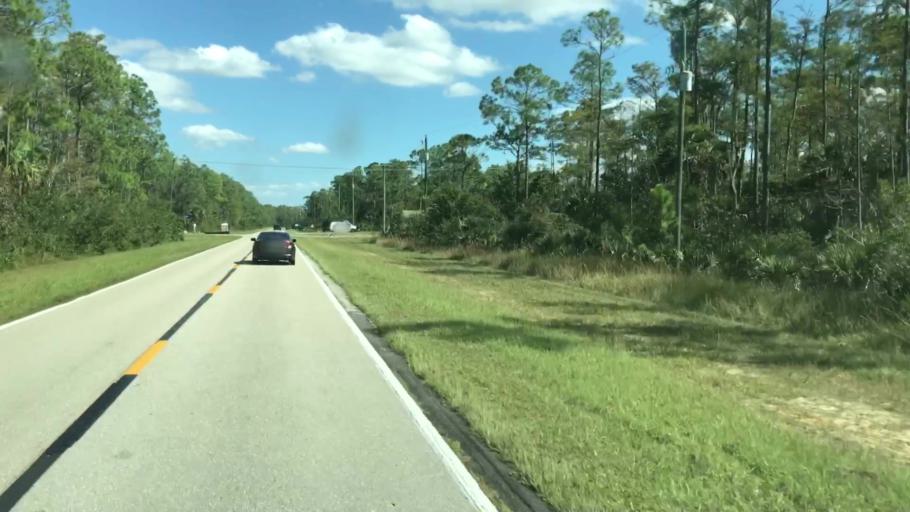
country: US
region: Florida
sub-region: Lee County
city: Alva
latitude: 26.6775
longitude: -81.6126
